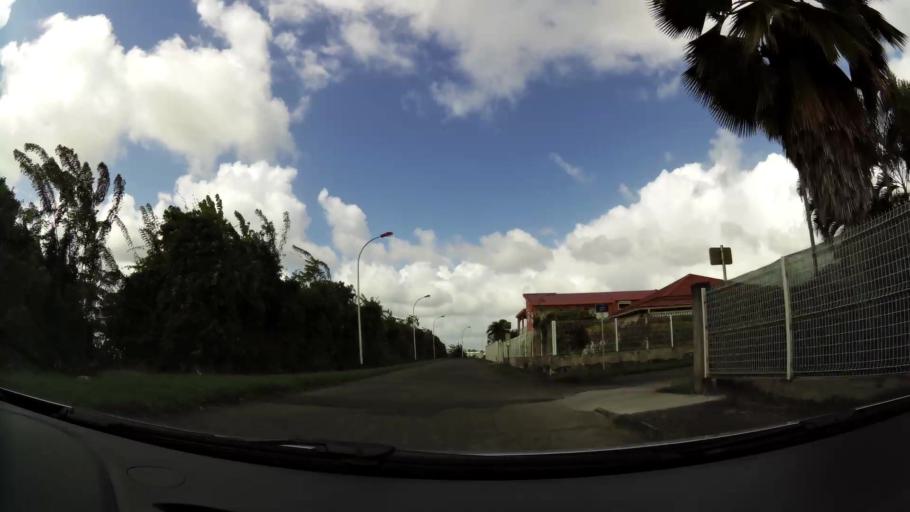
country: MQ
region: Martinique
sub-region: Martinique
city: Le Lamentin
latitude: 14.6136
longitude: -60.9876
